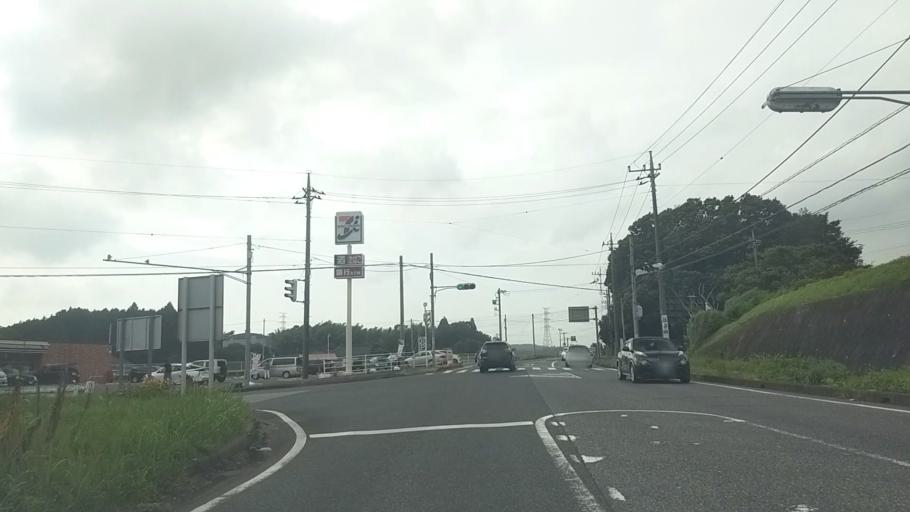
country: JP
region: Chiba
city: Kimitsu
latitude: 35.2774
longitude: 139.9923
